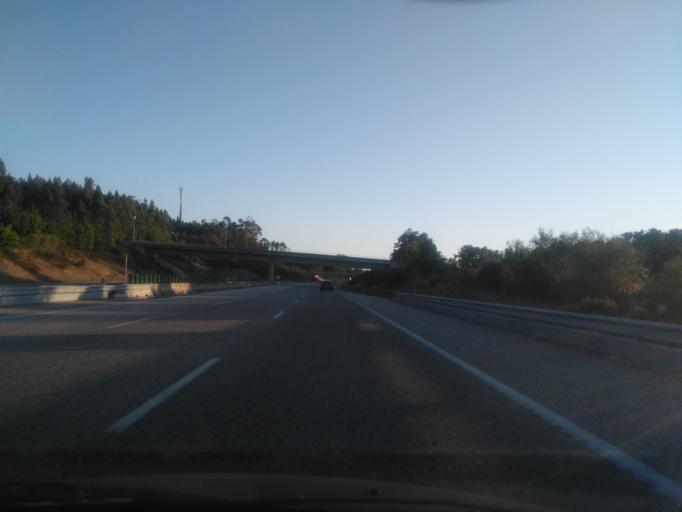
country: PT
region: Leiria
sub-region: Leiria
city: Monte Redondo
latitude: 39.9302
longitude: -8.7797
